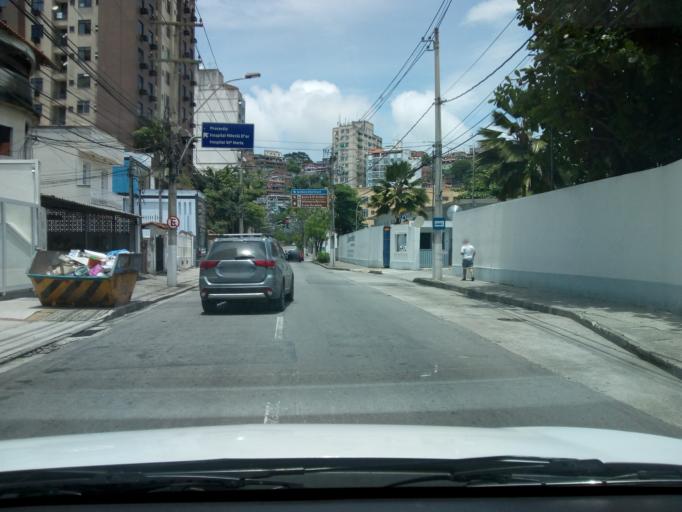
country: BR
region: Rio de Janeiro
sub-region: Niteroi
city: Niteroi
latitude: -22.9085
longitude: -43.1034
